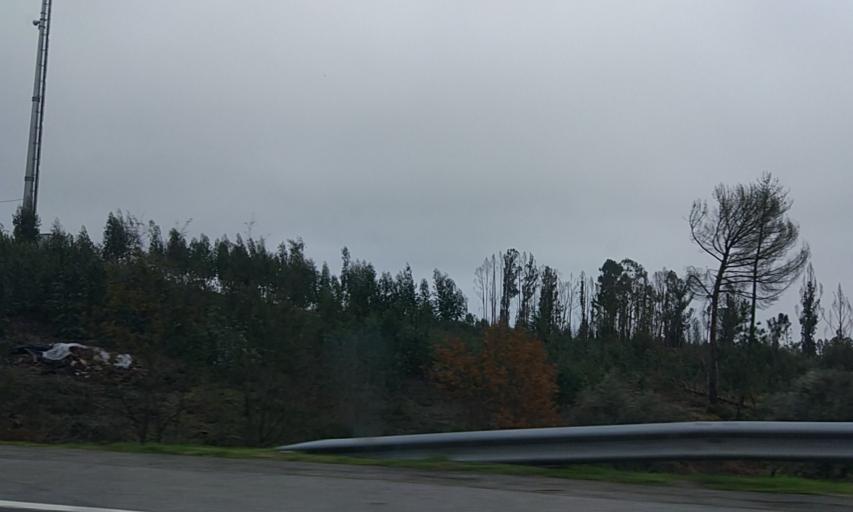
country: PT
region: Viseu
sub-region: Concelho de Tondela
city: Tondela
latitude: 40.5688
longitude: -8.0379
